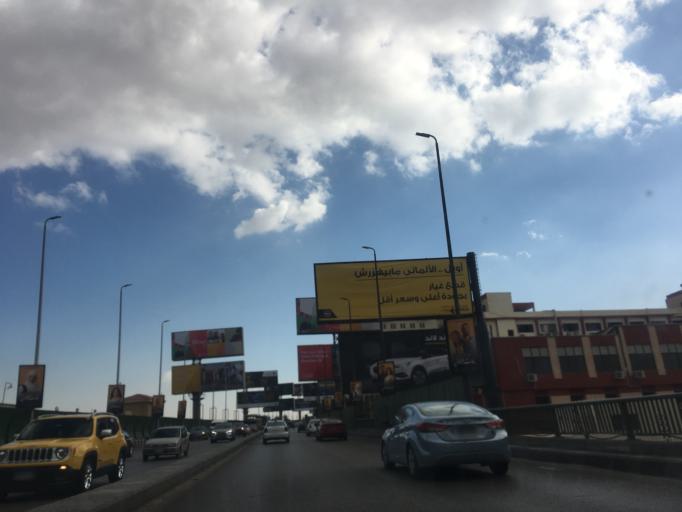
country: EG
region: Muhafazat al Qahirah
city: Cairo
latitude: 30.0726
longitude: 31.2882
